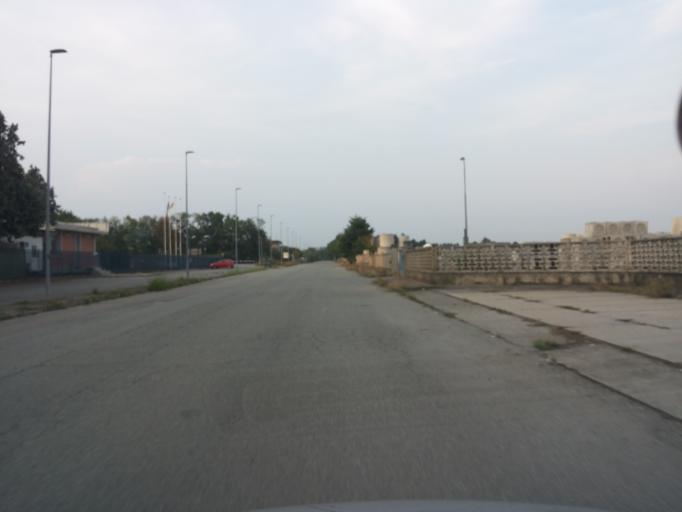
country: IT
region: Piedmont
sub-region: Provincia di Biella
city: Cavaglia
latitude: 45.3864
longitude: 8.1223
